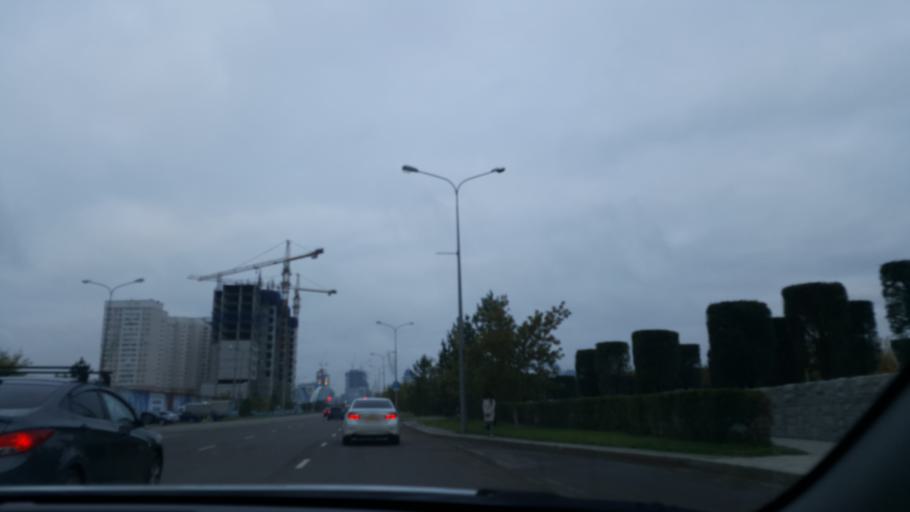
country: KZ
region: Astana Qalasy
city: Astana
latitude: 51.1204
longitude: 71.4634
